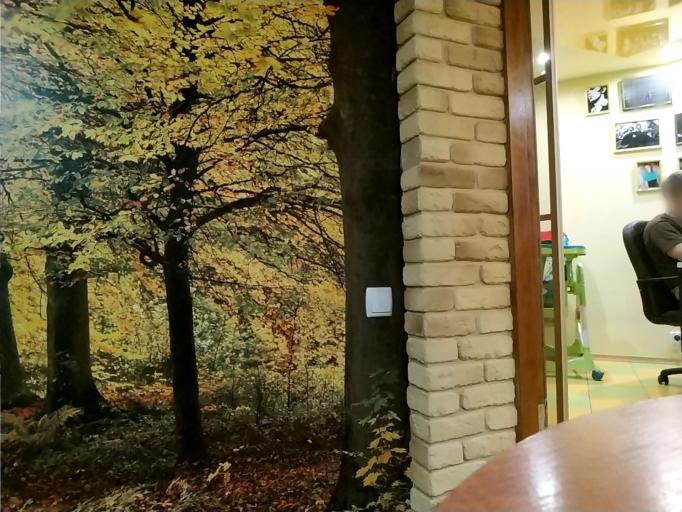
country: RU
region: Tverskaya
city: Zapadnaya Dvina
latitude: 56.3278
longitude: 31.8994
